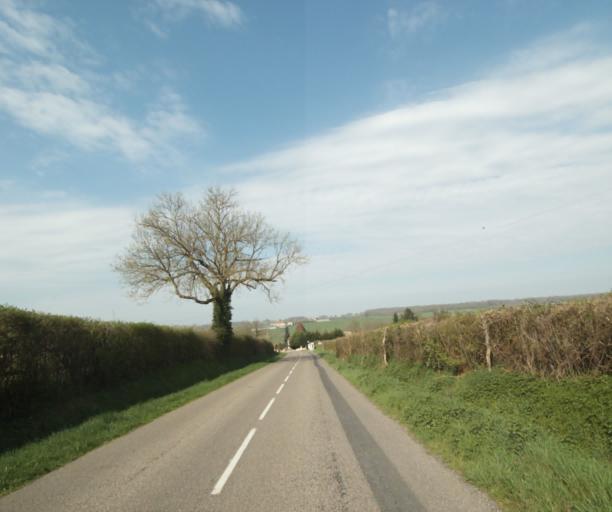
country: FR
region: Bourgogne
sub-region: Departement de Saone-et-Loire
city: Palinges
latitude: 46.5060
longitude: 4.1899
